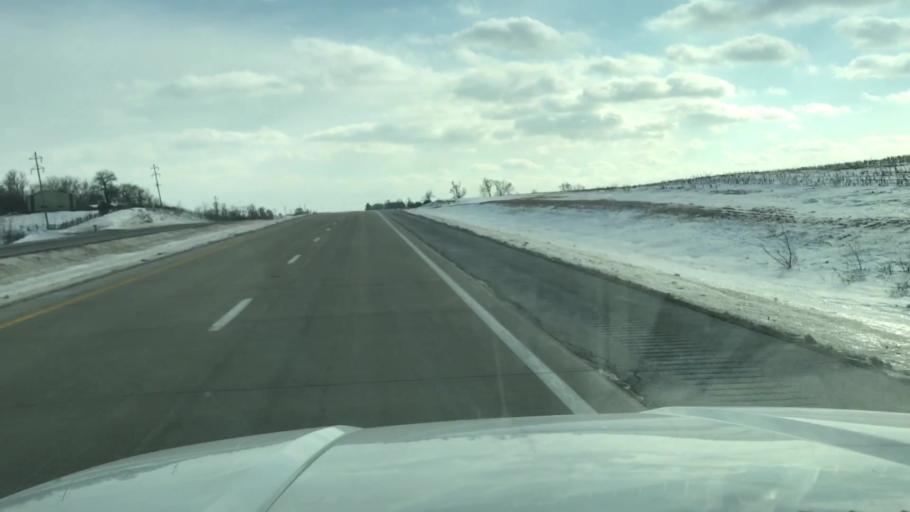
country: US
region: Missouri
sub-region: Nodaway County
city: Maryville
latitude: 40.2209
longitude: -94.8681
